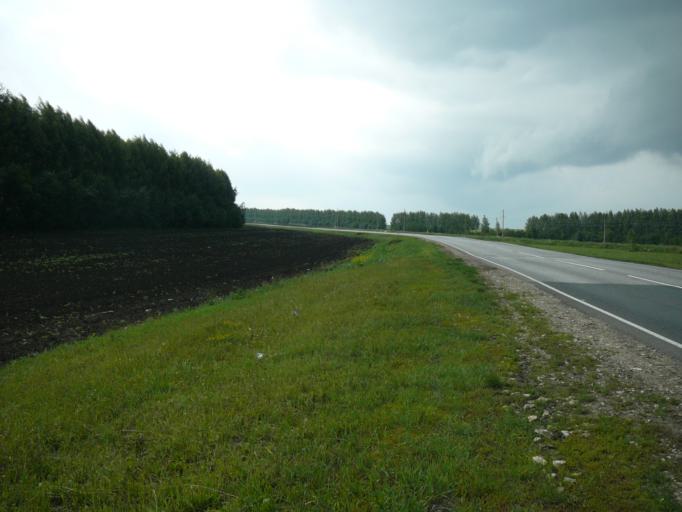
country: RU
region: Penza
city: Issa
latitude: 53.7370
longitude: 44.7658
